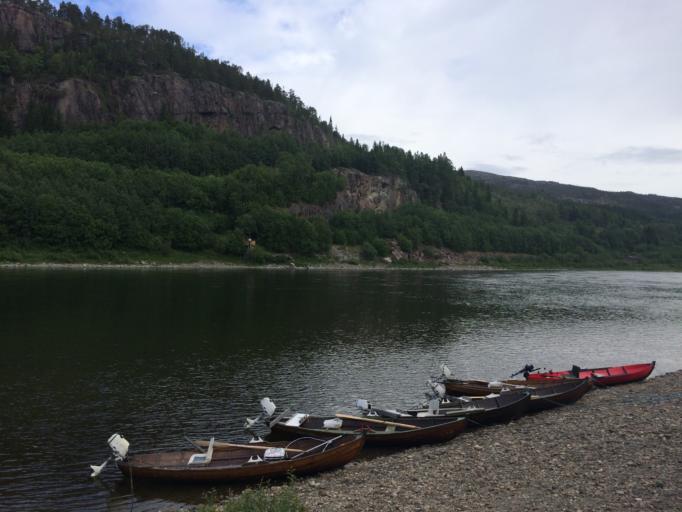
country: NO
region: Nord-Trondelag
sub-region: Overhalla
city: Ranemsletta
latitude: 64.4667
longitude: 12.0599
